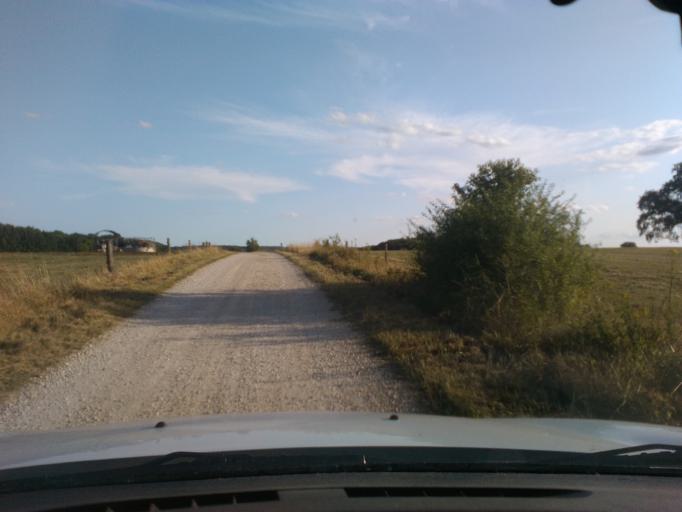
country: FR
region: Lorraine
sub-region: Departement des Vosges
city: Mirecourt
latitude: 48.3455
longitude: 6.0315
